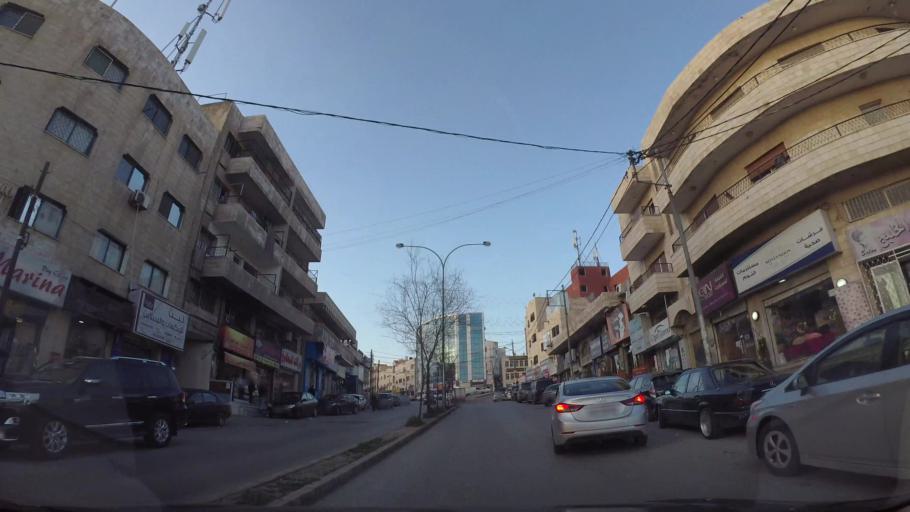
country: JO
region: Amman
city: Amman
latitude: 31.9966
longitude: 35.9459
